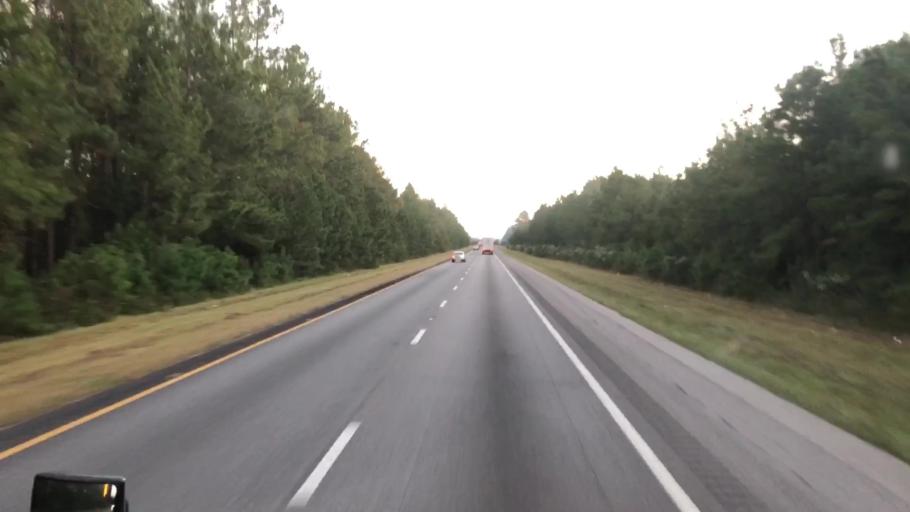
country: US
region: South Carolina
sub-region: Orangeburg County
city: Holly Hill
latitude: 33.3656
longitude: -80.5248
